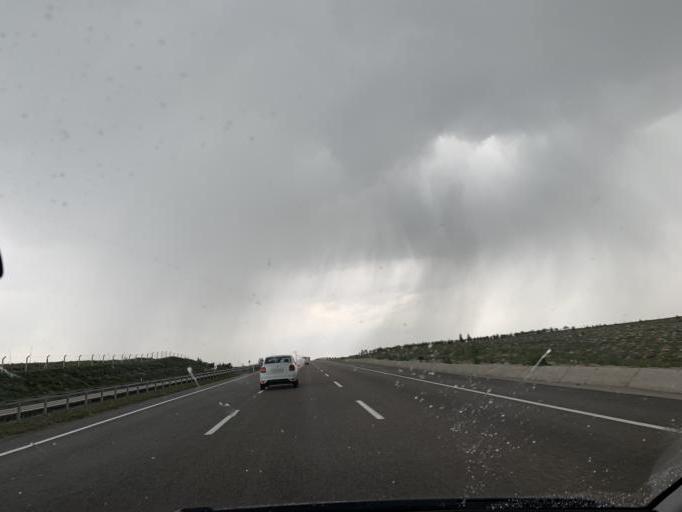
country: TR
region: Eskisehir
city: Gunyuzu
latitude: 39.5755
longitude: 31.9176
